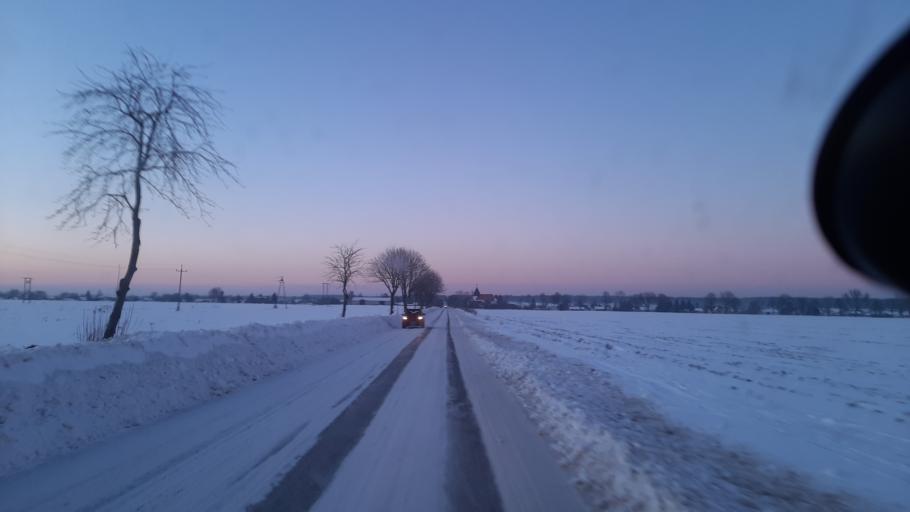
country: PL
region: Lublin Voivodeship
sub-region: Powiat lubelski
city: Niemce
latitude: 51.3551
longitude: 22.5358
